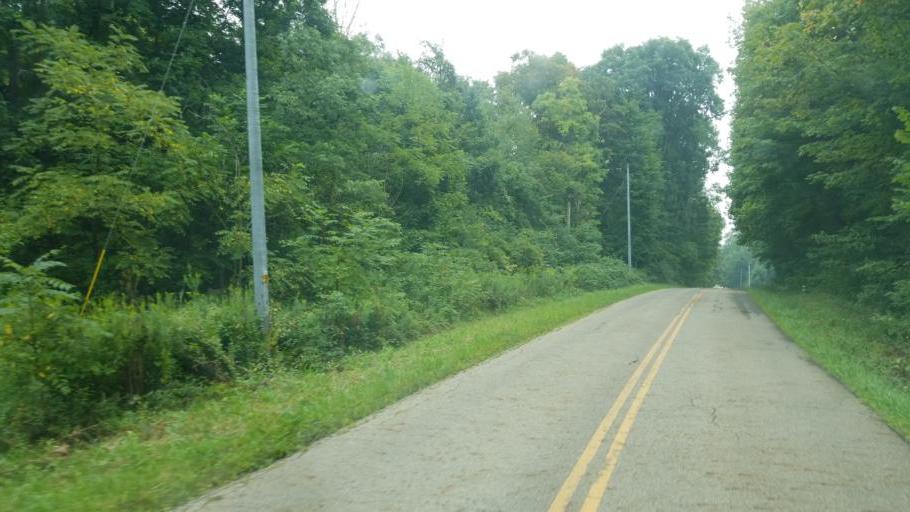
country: US
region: Ohio
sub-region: Licking County
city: Utica
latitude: 40.3130
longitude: -82.4557
